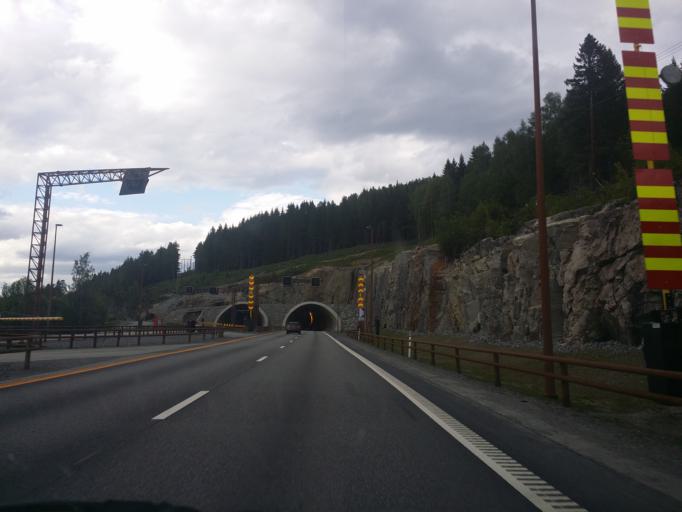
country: NO
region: Akershus
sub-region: Eidsvoll
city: Eidsvoll
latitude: 60.4622
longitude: 11.2440
